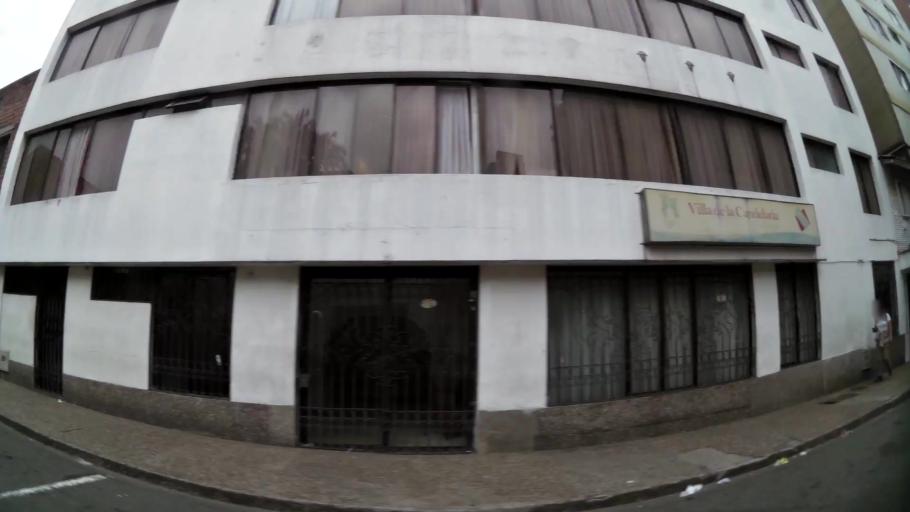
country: CO
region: Antioquia
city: Medellin
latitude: 6.2477
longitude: -75.5617
